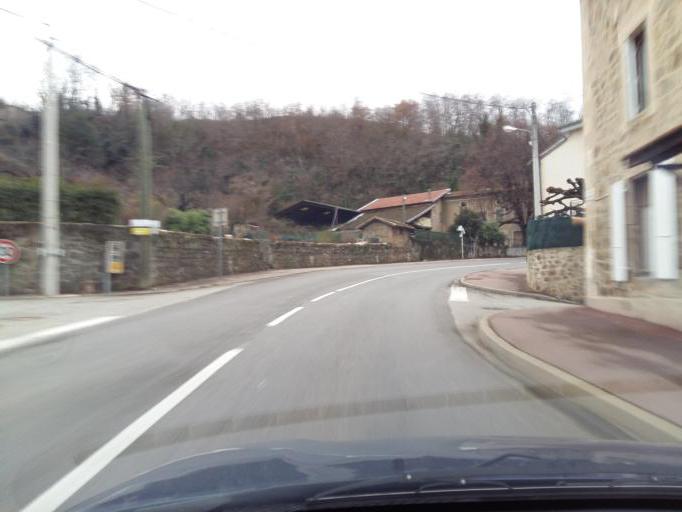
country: FR
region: Rhone-Alpes
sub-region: Departement de l'Ardeche
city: Andance
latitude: 45.2493
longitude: 4.7722
